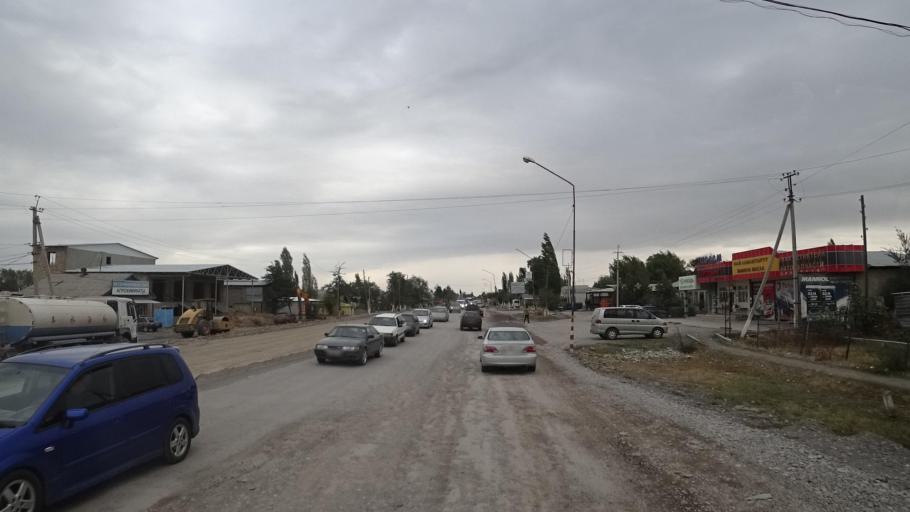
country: KG
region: Chuy
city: Sokuluk
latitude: 42.8542
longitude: 74.2332
